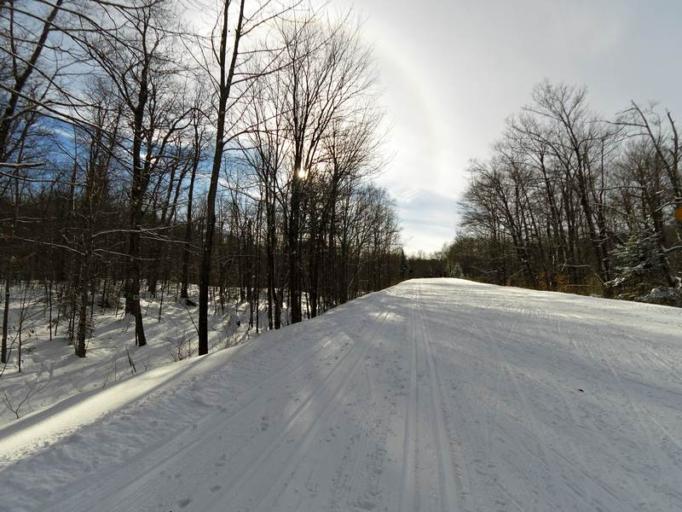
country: CA
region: Quebec
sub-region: Outaouais
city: Wakefield
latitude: 45.5040
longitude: -75.8850
